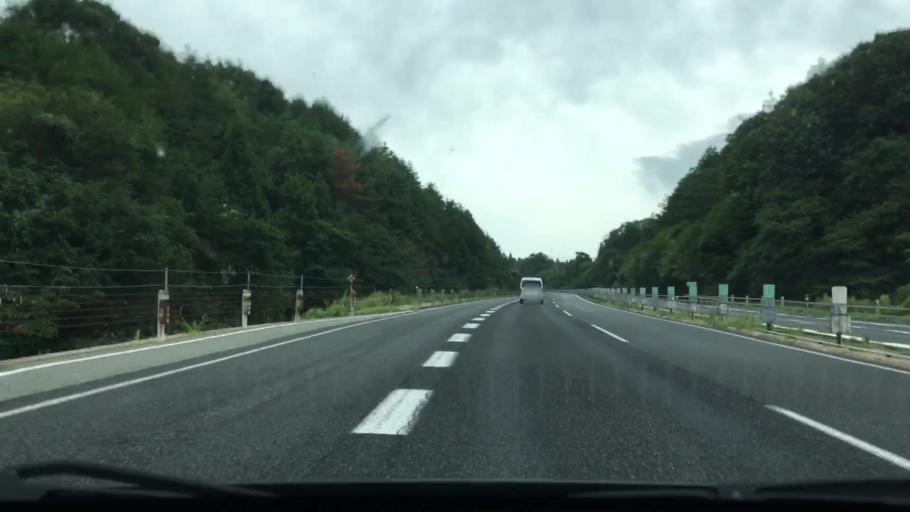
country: JP
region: Hiroshima
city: Hiroshima-shi
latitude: 34.6317
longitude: 132.5132
